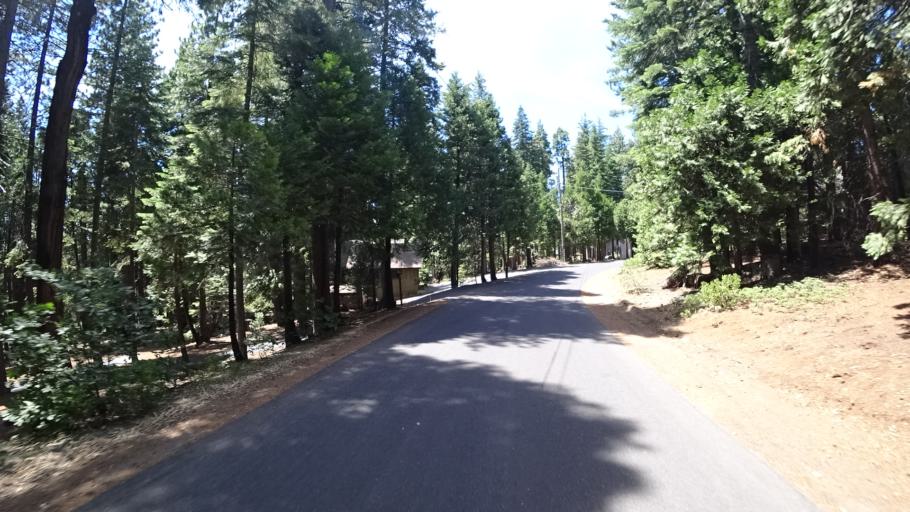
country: US
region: California
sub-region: Calaveras County
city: Arnold
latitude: 38.3100
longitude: -120.2675
